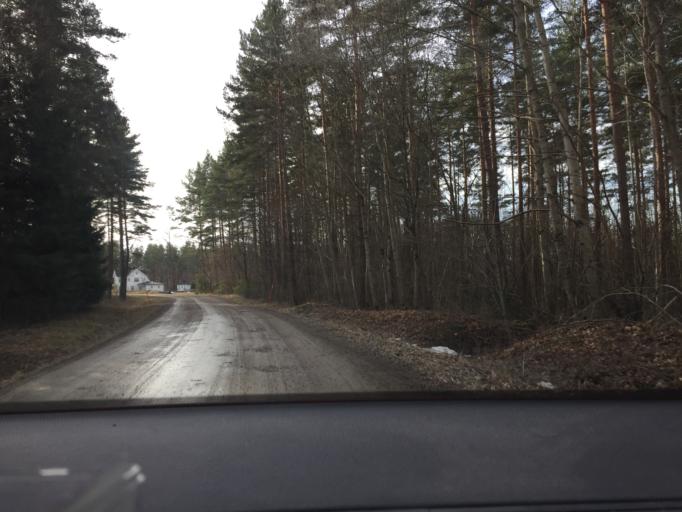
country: SE
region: OErebro
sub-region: Orebro Kommun
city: Odensbacken
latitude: 59.1169
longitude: 15.4681
